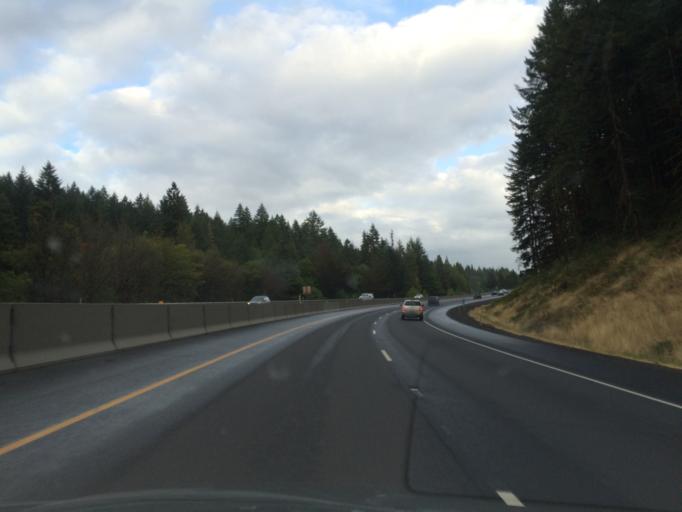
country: US
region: Oregon
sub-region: Lane County
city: Cottage Grove
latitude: 43.7537
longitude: -123.1397
